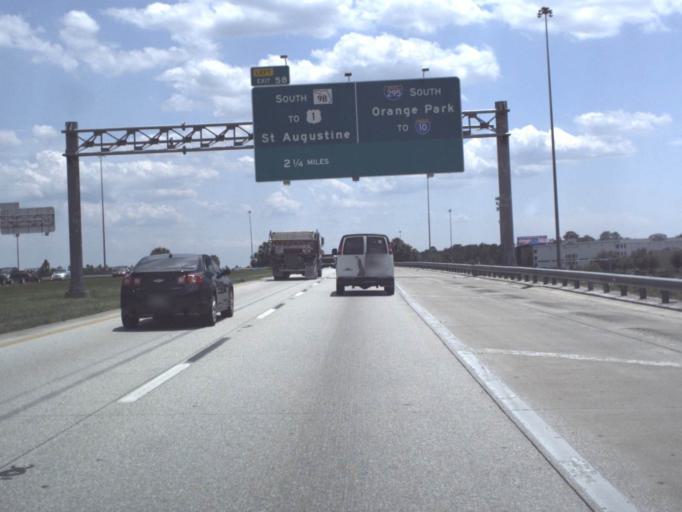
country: US
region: Florida
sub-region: Saint Johns County
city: Ponte Vedra Beach
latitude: 30.2184
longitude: -81.5142
